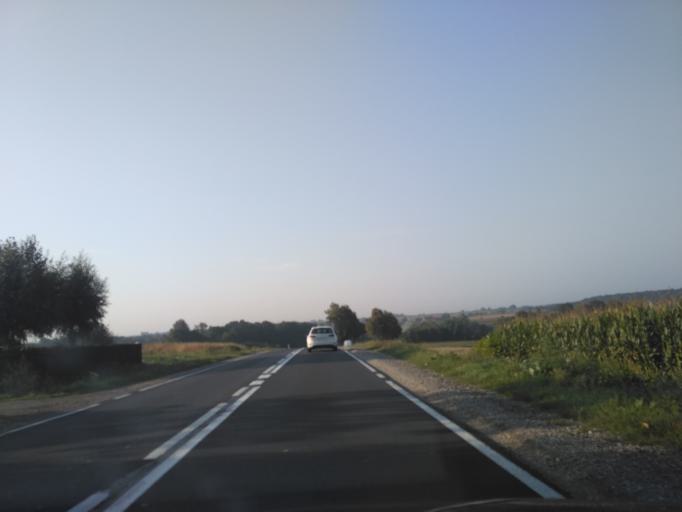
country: PL
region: Lublin Voivodeship
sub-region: Powiat krasnicki
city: Szastarka
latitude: 50.8065
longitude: 22.3198
